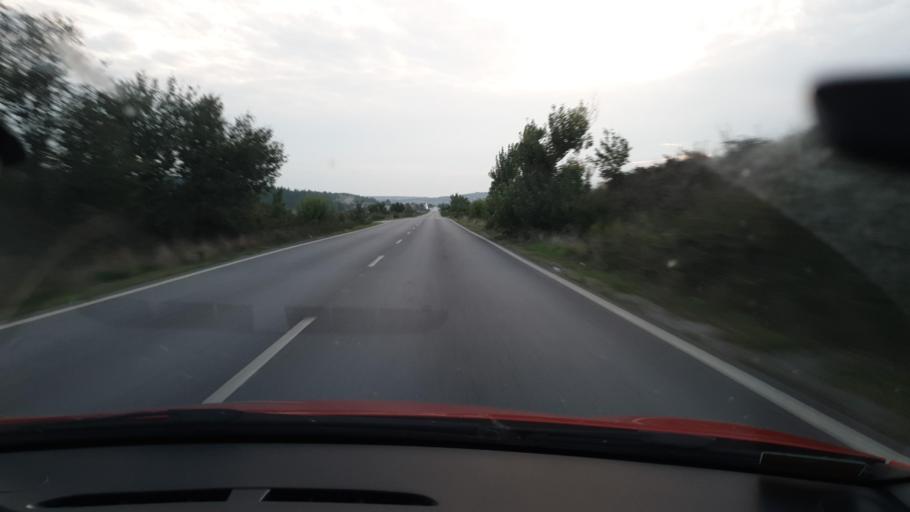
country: GR
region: Central Macedonia
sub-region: Nomos Kilkis
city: Kristoni
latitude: 41.0018
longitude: 22.7796
